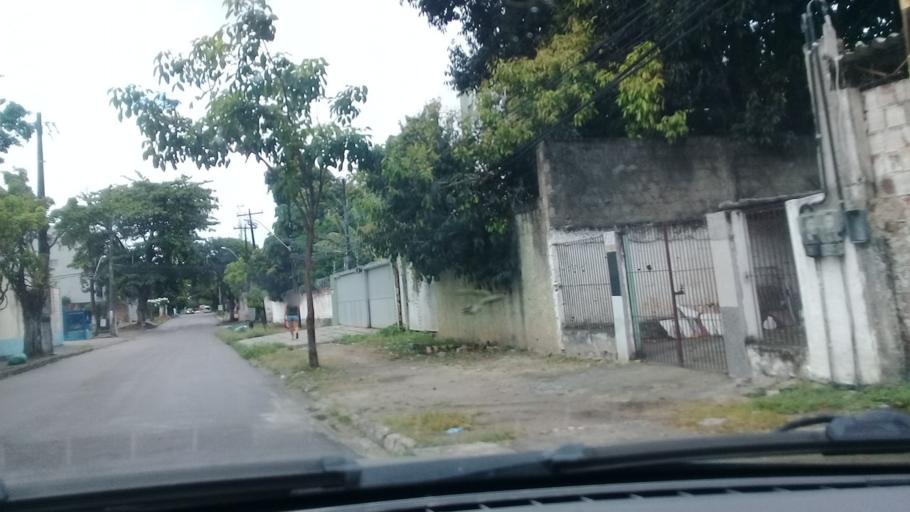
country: BR
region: Pernambuco
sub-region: Recife
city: Recife
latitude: -8.1412
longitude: -34.9150
